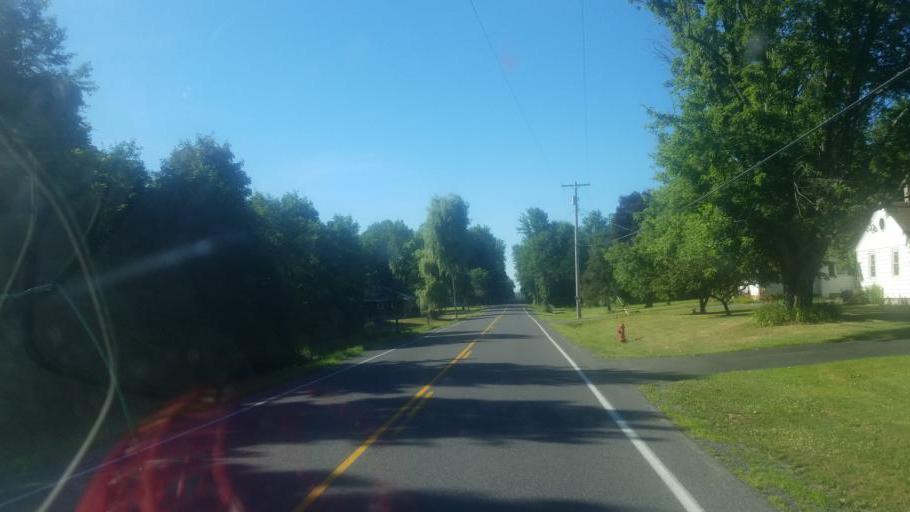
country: US
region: New York
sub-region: Ontario County
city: Phelps
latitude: 42.9231
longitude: -77.0655
